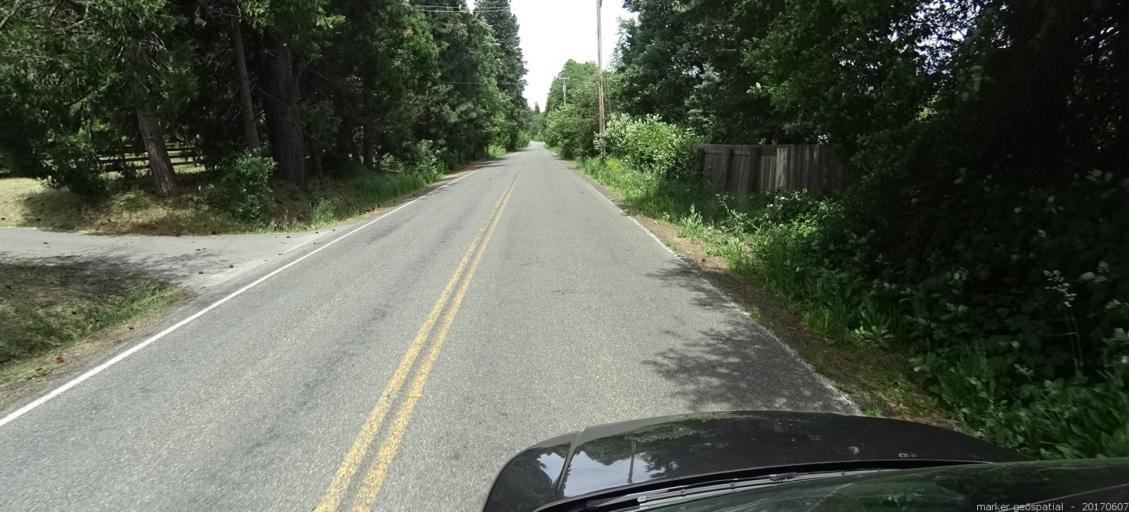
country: US
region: California
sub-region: Siskiyou County
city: Mount Shasta
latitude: 41.3020
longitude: -122.3242
